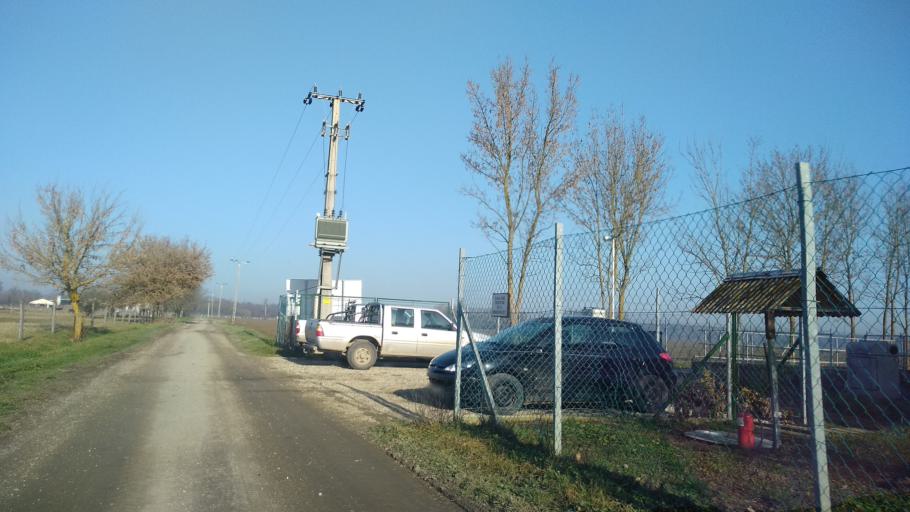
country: HU
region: Somogy
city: Barcs
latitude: 45.9479
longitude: 17.4882
